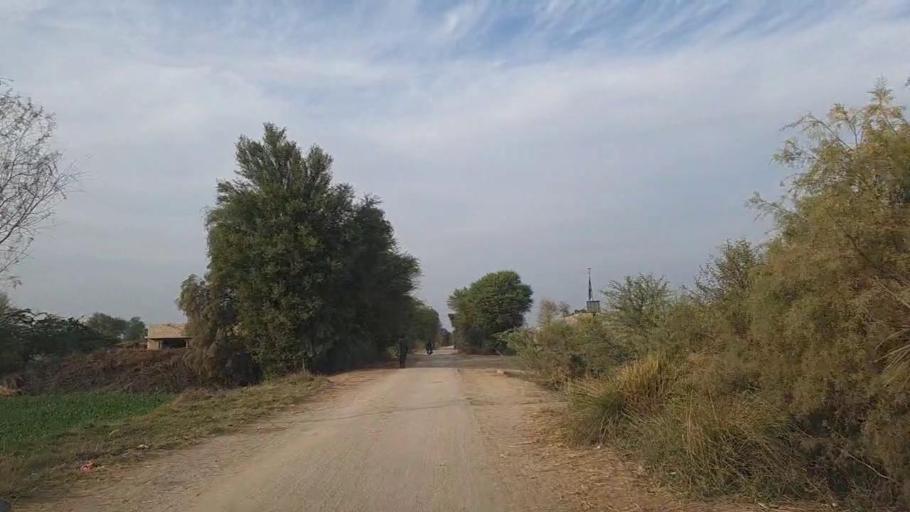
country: PK
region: Sindh
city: Daur
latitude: 26.5185
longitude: 68.4072
